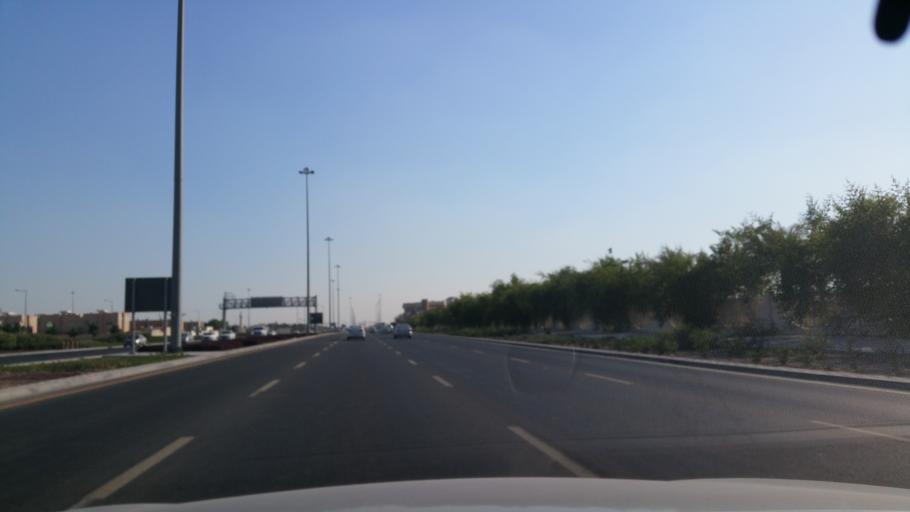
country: QA
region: Baladiyat ar Rayyan
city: Ar Rayyan
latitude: 25.2762
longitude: 51.4312
